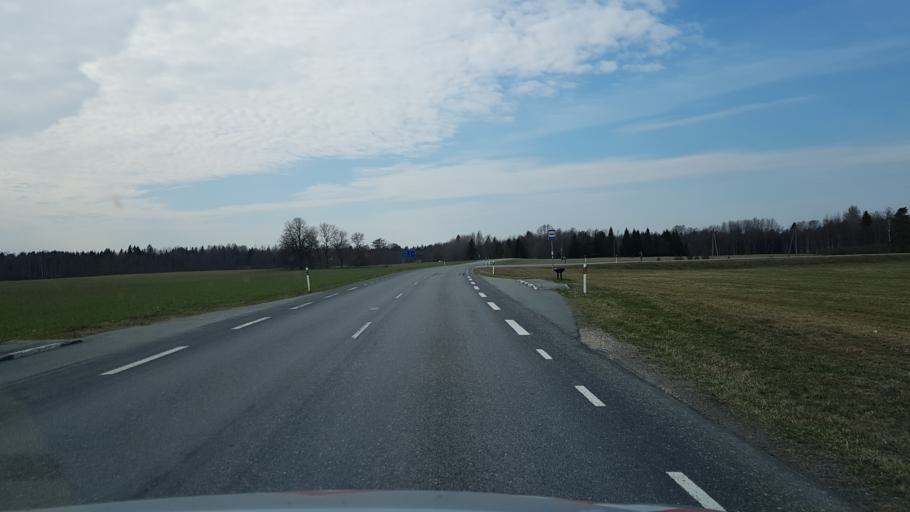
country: EE
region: Laeaene-Virumaa
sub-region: Haljala vald
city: Haljala
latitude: 59.4622
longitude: 26.1980
